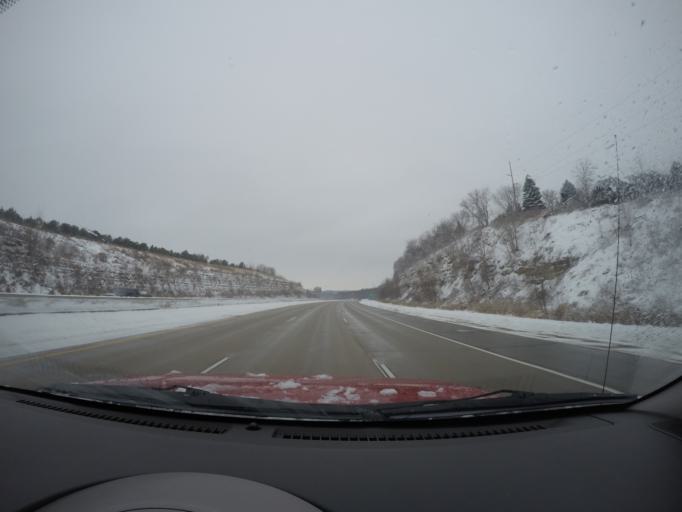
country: US
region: Minnesota
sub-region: Olmsted County
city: Rochester
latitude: 43.9856
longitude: -92.4779
